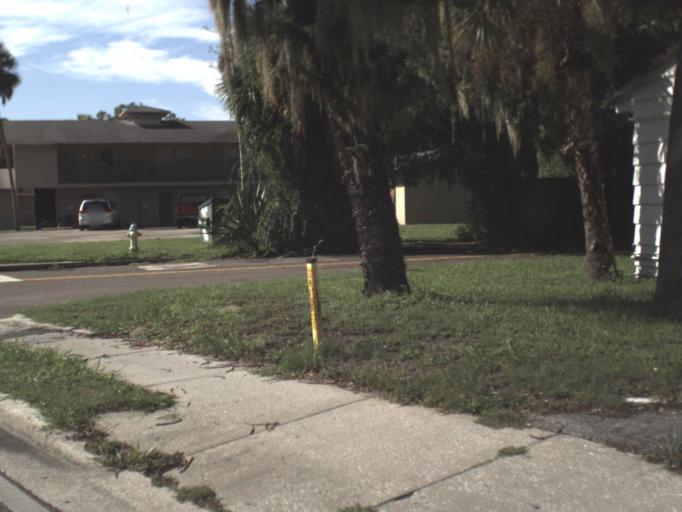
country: US
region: Florida
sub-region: Sarasota County
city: Sarasota
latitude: 27.3581
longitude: -82.5486
